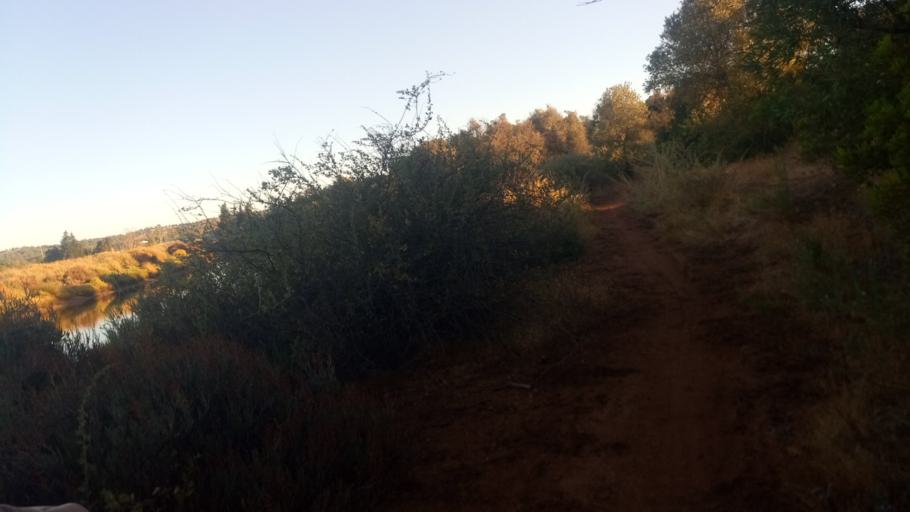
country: PT
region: Faro
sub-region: Tavira
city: Tavira
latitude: 37.1423
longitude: -7.6161
